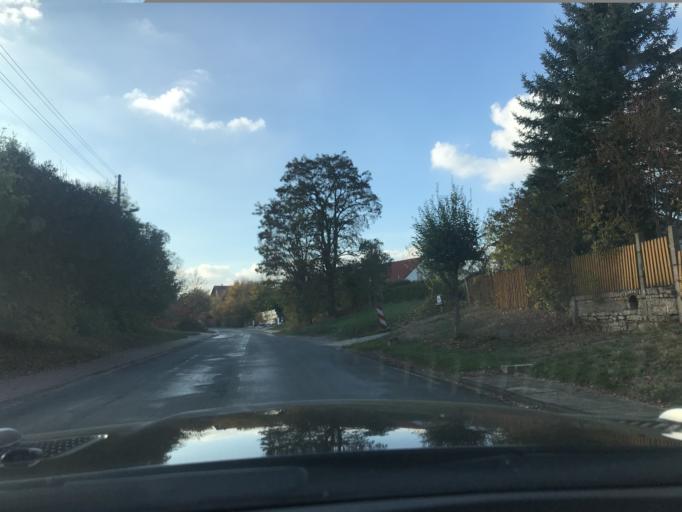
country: DE
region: Thuringia
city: Mulverstedt
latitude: 51.1188
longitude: 10.5023
